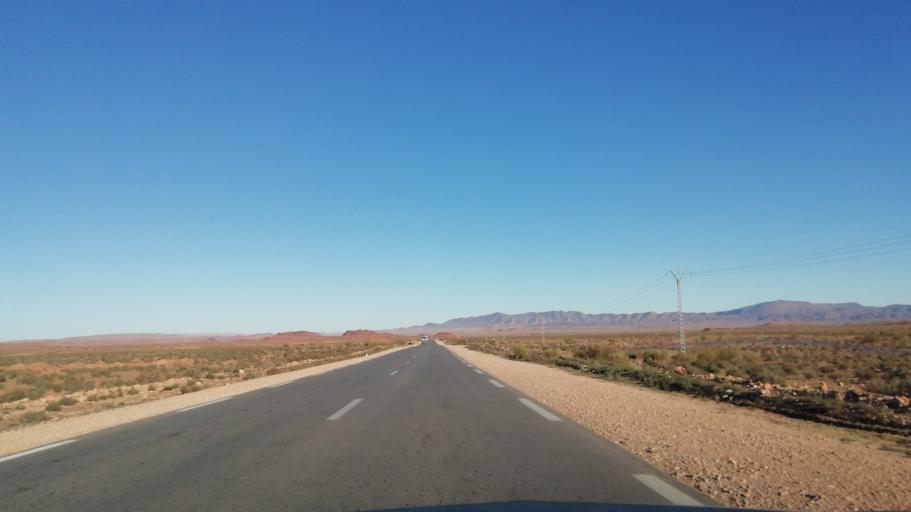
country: DZ
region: El Bayadh
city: El Abiodh Sidi Cheikh
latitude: 33.1690
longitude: 0.4809
